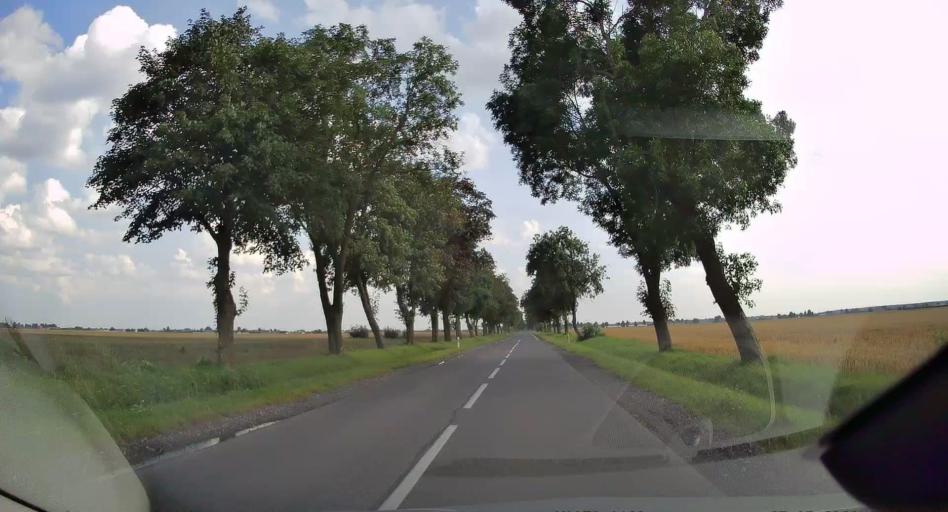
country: PL
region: Lodz Voivodeship
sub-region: Powiat tomaszowski
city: Rzeczyca
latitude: 51.6224
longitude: 20.2929
